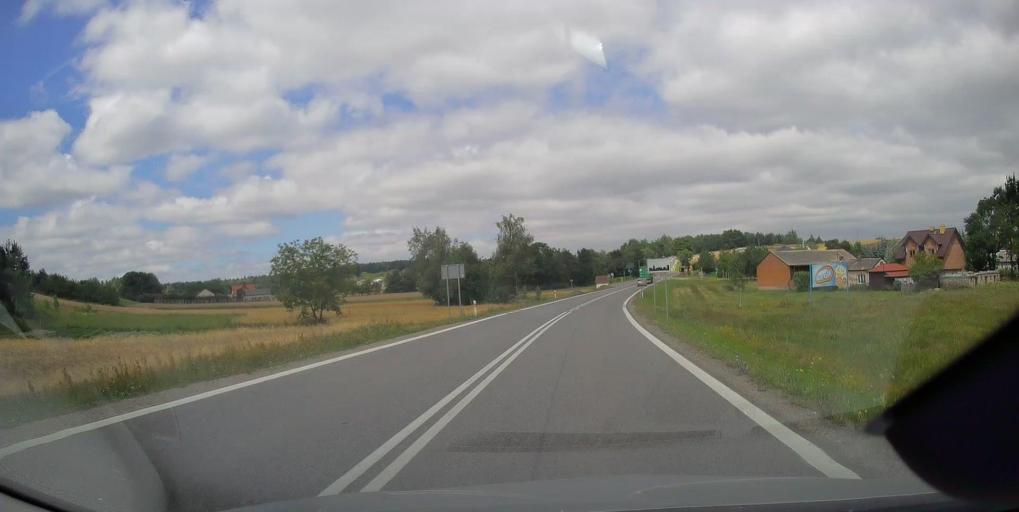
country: PL
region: Swietokrzyskie
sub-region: Powiat sandomierski
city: Klimontow
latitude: 50.6322
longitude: 21.4708
